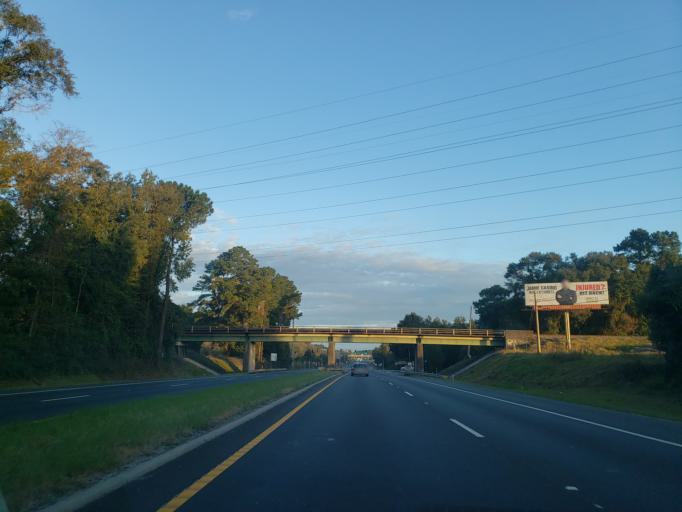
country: US
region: Georgia
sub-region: Chatham County
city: Port Wentworth
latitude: 32.1525
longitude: -81.1802
